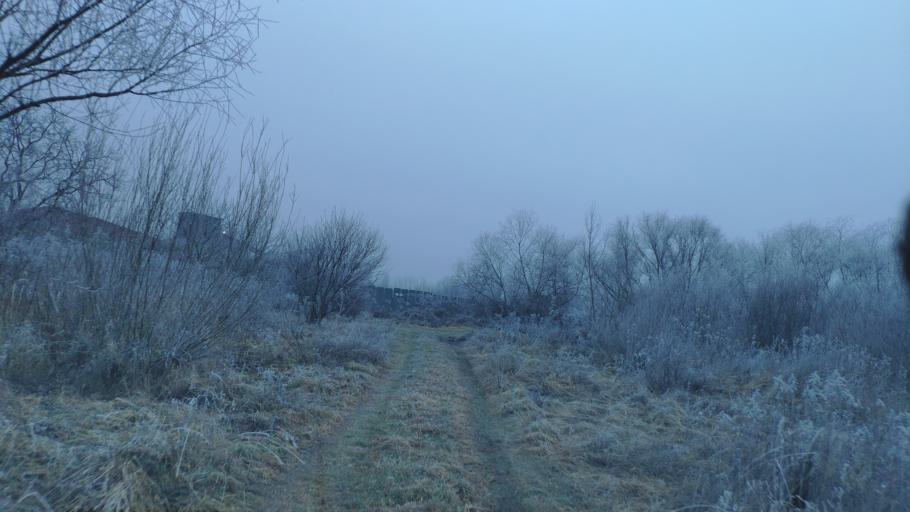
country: SK
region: Kosicky
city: Kosice
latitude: 48.6200
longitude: 21.3246
